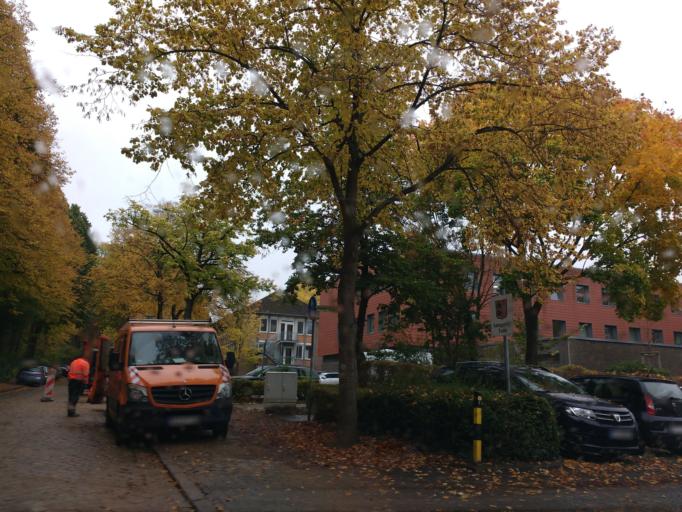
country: DE
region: Schleswig-Holstein
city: Eutin
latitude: 54.1347
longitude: 10.6196
